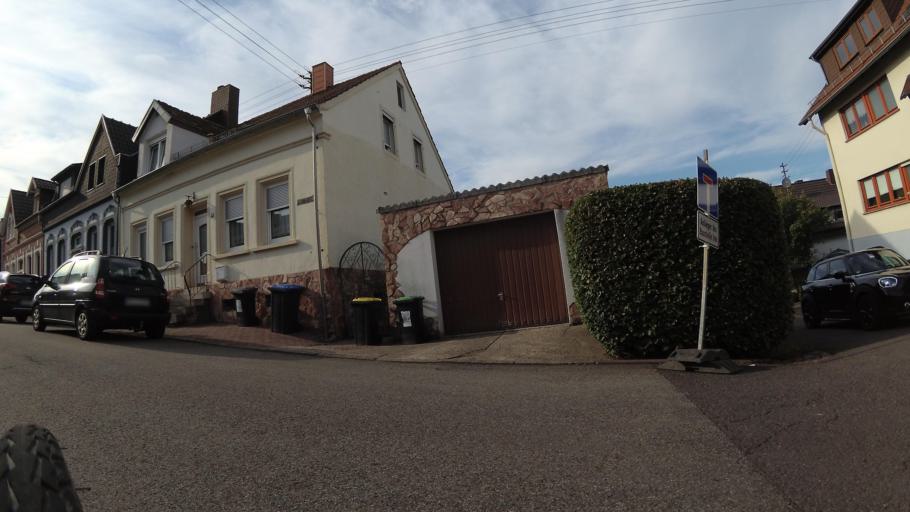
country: DE
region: Saarland
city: Friedrichsthal
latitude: 49.3345
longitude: 7.0940
